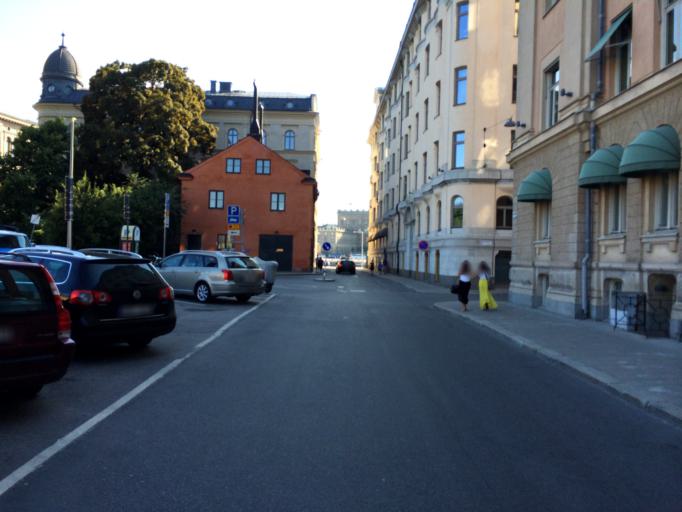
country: SE
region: Stockholm
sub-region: Stockholms Kommun
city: OEstermalm
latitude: 59.3298
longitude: 18.0782
